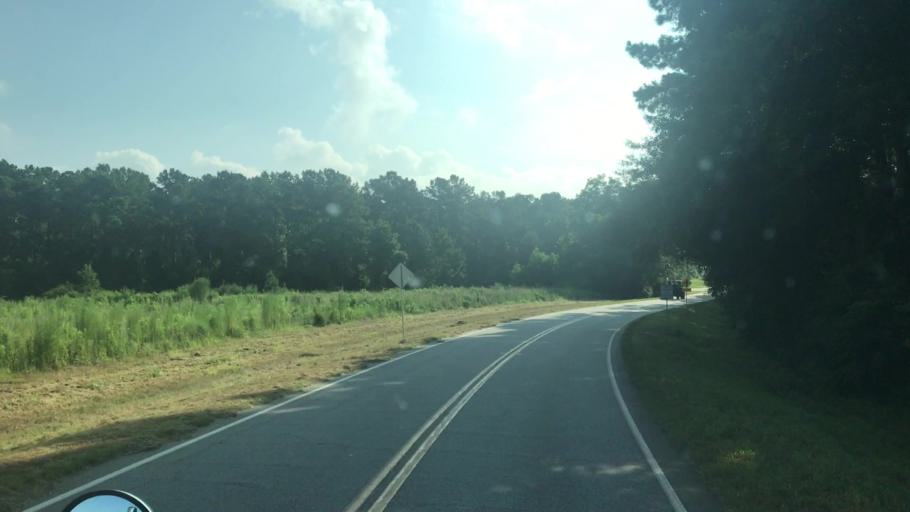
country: US
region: Florida
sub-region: Gadsden County
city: Quincy
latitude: 30.6975
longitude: -84.5361
